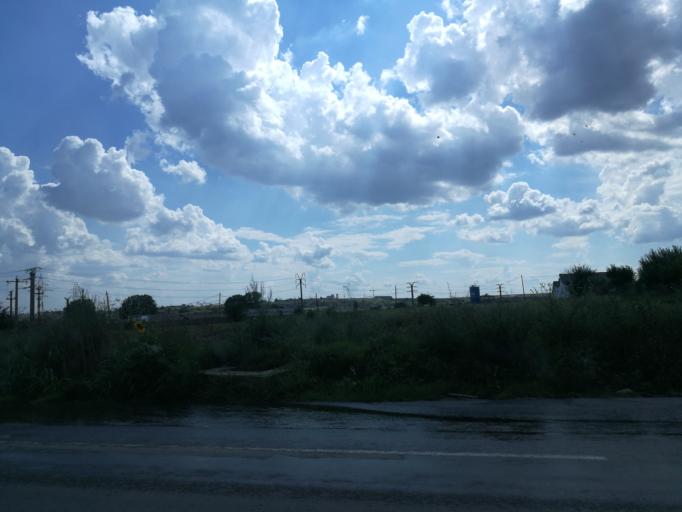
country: RO
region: Constanta
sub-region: Comuna Ovidiu
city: Ovidiu
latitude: 44.2737
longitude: 28.5573
